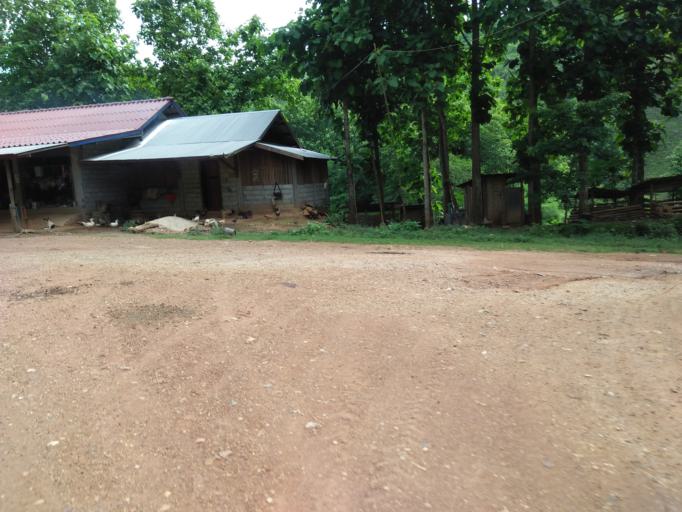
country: TH
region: Chiang Rai
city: Wiang Kaen
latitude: 19.8318
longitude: 100.7152
